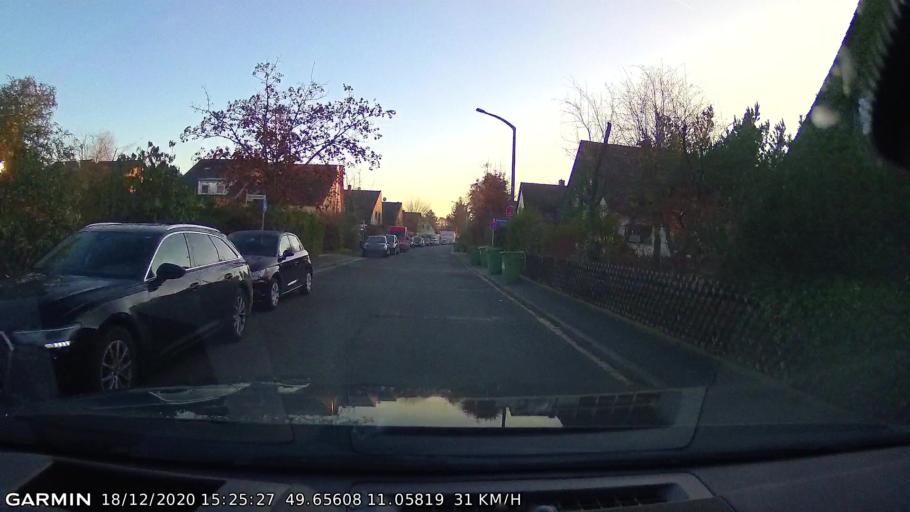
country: DE
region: Bavaria
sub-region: Upper Franconia
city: Poxdorf
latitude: 49.6561
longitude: 11.0581
